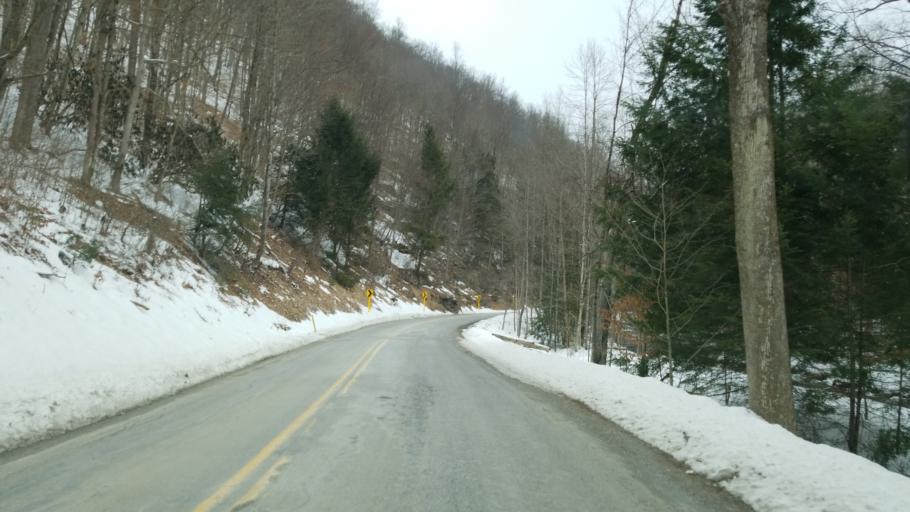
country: US
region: Pennsylvania
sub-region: Cameron County
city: Emporium
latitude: 41.2736
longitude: -78.1444
